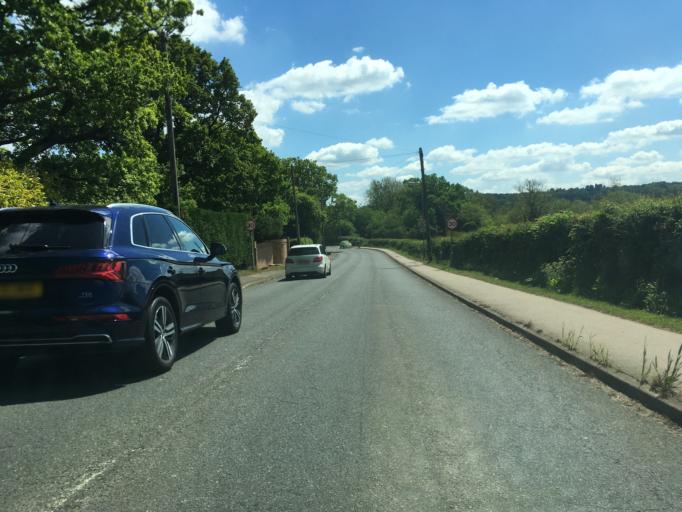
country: GB
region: England
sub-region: Milton Keynes
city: Woburn Sands
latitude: 52.0201
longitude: -0.6572
